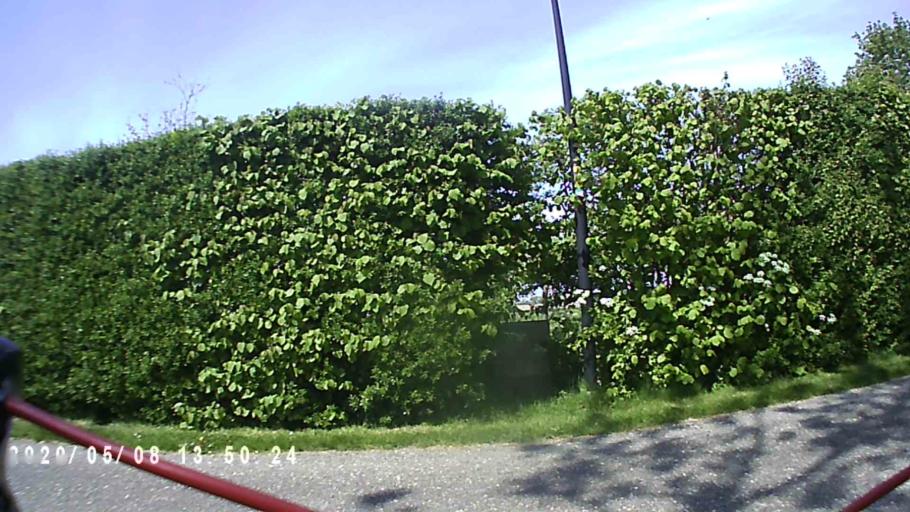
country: NL
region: Groningen
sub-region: Gemeente Appingedam
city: Appingedam
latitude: 53.3404
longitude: 6.7783
